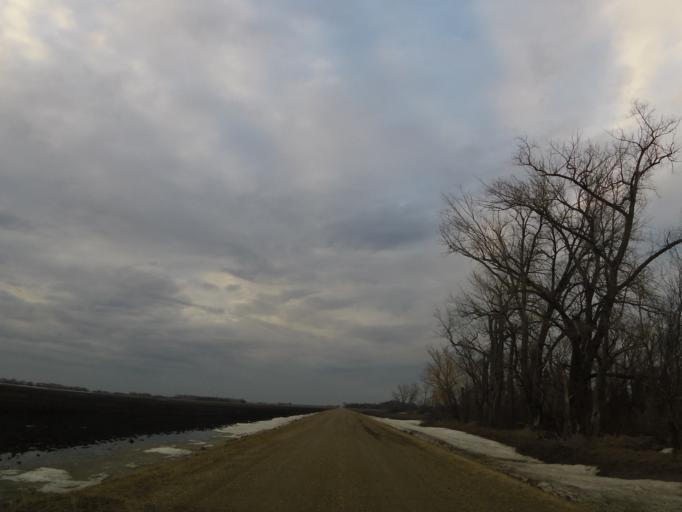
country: US
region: North Dakota
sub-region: Walsh County
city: Grafton
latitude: 48.3909
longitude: -97.2119
